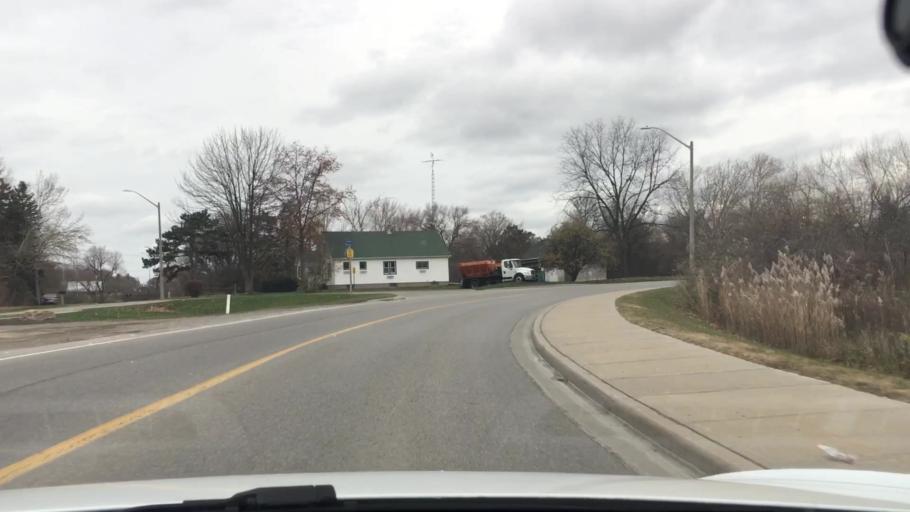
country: CA
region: Ontario
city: Oshawa
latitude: 43.8881
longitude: -78.8221
